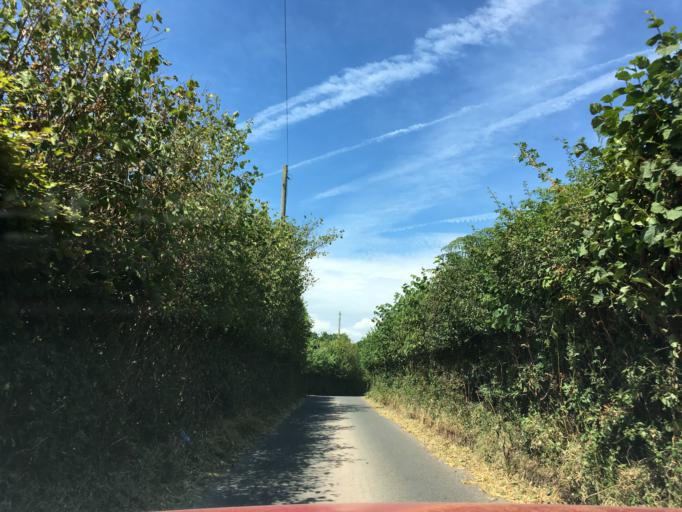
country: GB
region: Wales
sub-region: Caerphilly County Borough
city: Machen
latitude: 51.5544
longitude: -3.1444
